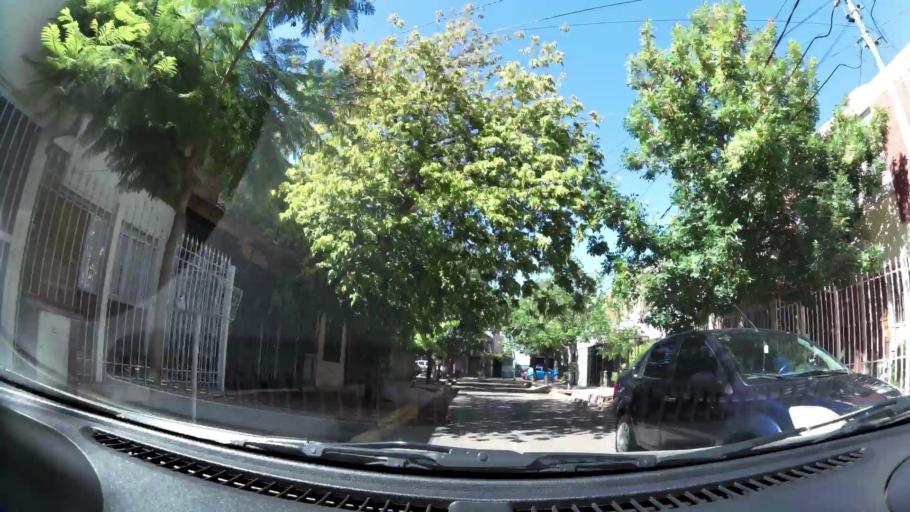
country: AR
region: Mendoza
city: Mendoza
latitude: -32.9032
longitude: -68.8578
